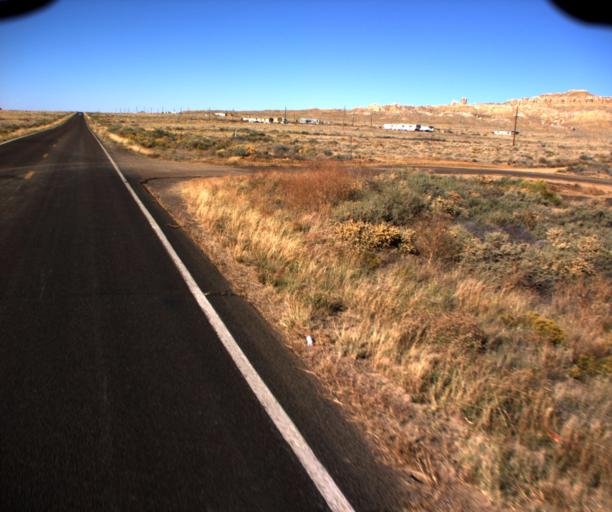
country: US
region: Arizona
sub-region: Navajo County
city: First Mesa
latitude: 35.7959
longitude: -110.4689
